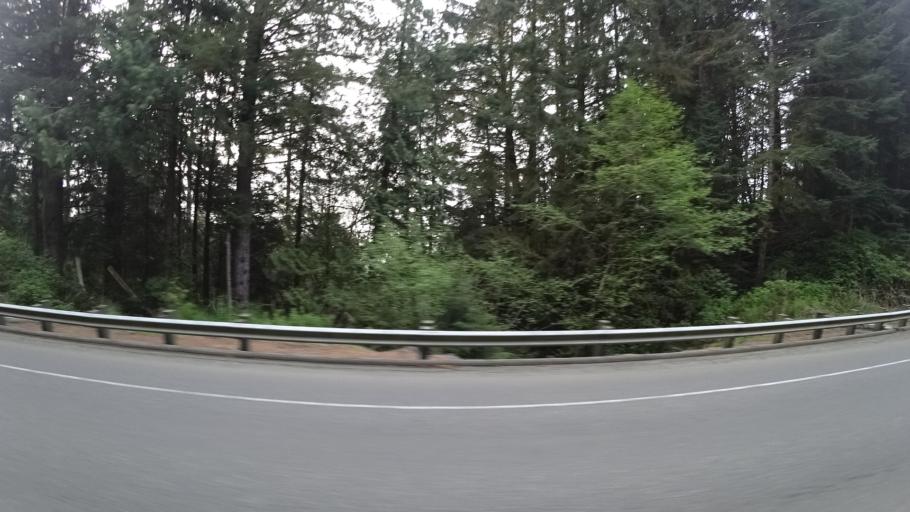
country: US
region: Oregon
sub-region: Coos County
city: Barview
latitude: 43.2539
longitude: -124.2856
